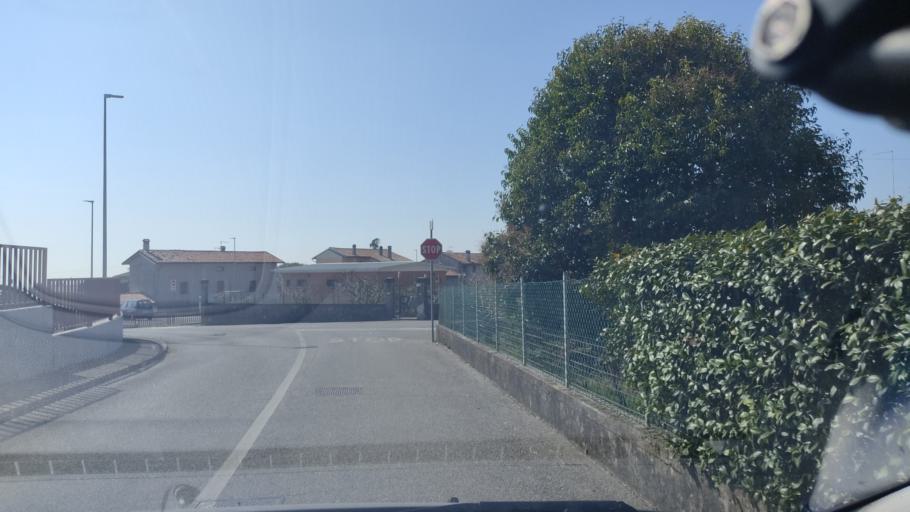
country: IT
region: Friuli Venezia Giulia
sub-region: Provincia di Pordenone
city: Budoia
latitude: 46.0454
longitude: 12.5357
